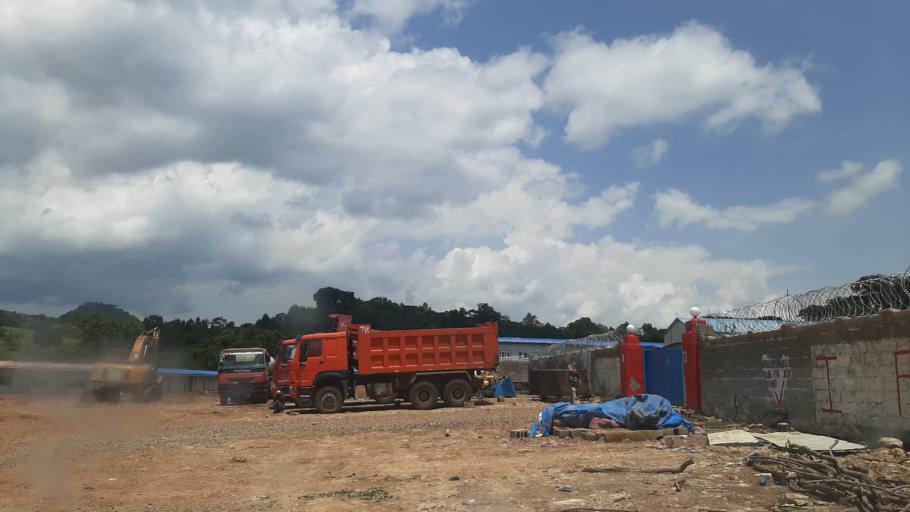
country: ET
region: Oromiya
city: Agaro
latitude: 7.9413
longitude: 36.8405
